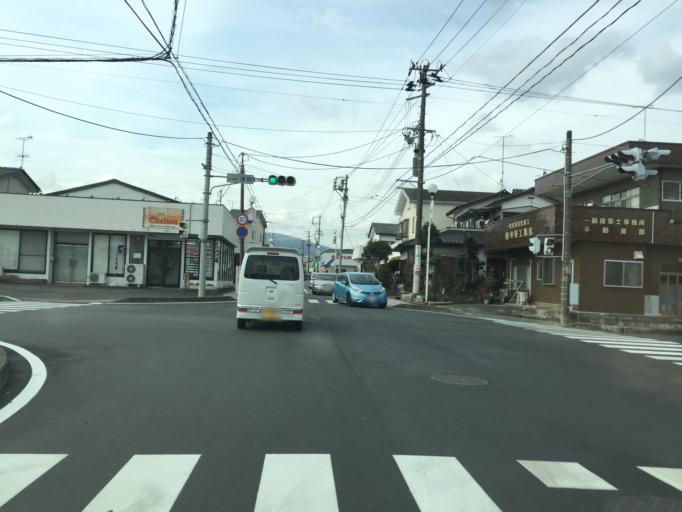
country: JP
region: Ibaraki
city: Kitaibaraki
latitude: 36.8900
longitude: 140.7662
